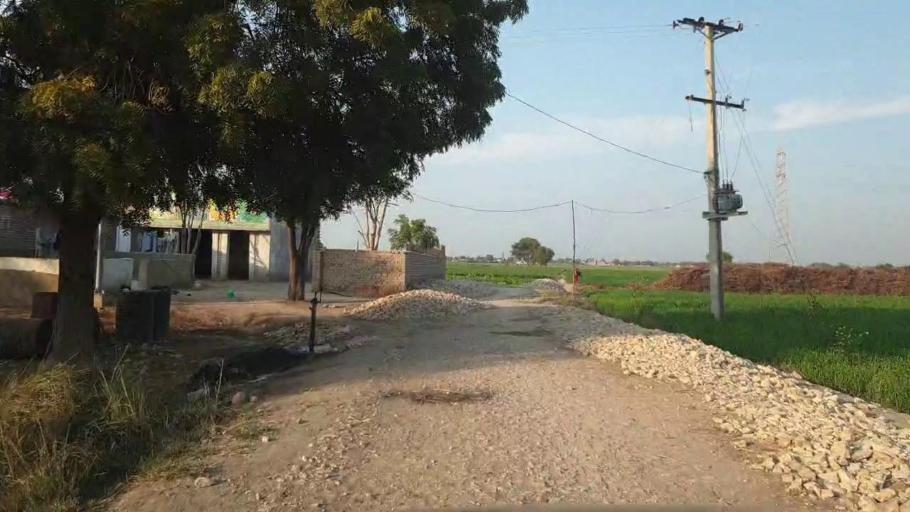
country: PK
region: Sindh
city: Shahpur Chakar
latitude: 26.1546
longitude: 68.6174
